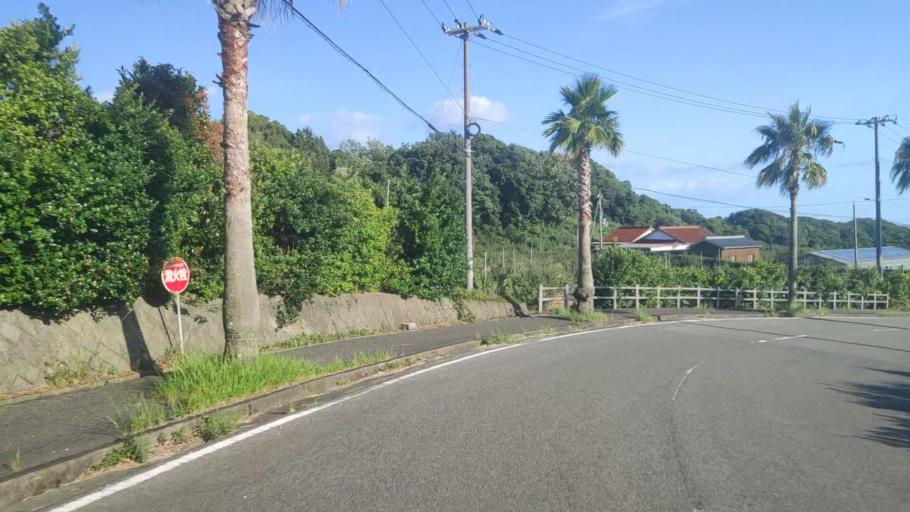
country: JP
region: Wakayama
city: Tanabe
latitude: 33.7724
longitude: 135.3062
